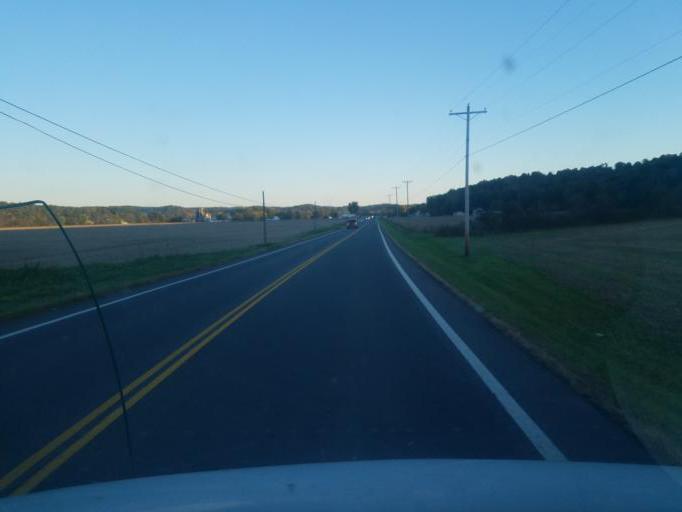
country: US
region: Ohio
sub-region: Licking County
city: Utica
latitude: 40.1928
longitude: -82.4306
